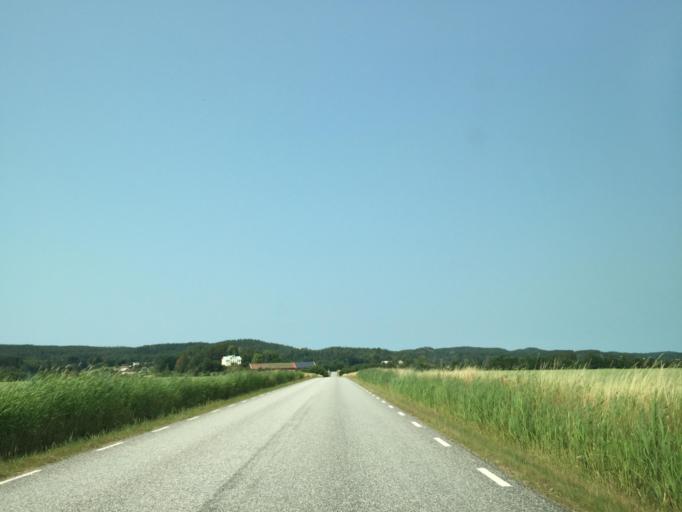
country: SE
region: Vaestra Goetaland
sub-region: Lilla Edets Kommun
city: Lilla Edet
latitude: 58.1908
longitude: 12.1175
